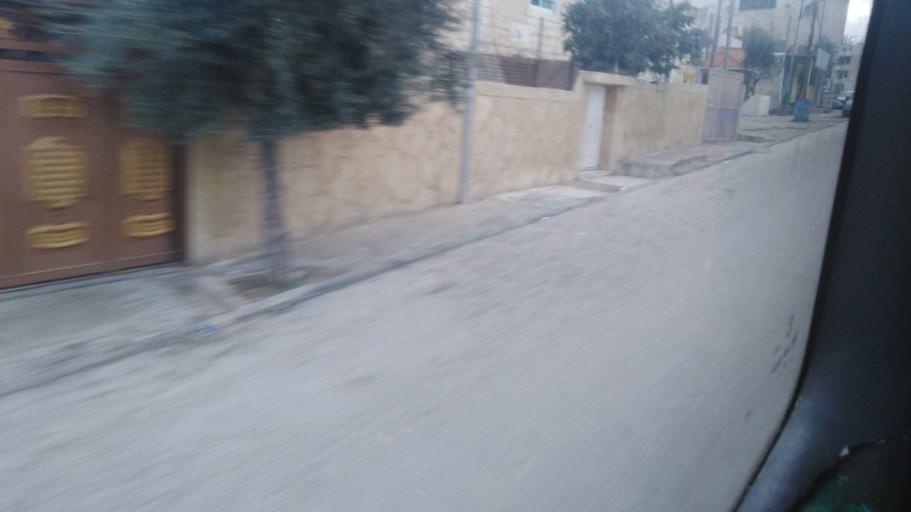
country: PS
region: West Bank
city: Hebron
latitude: 31.5278
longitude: 35.0861
